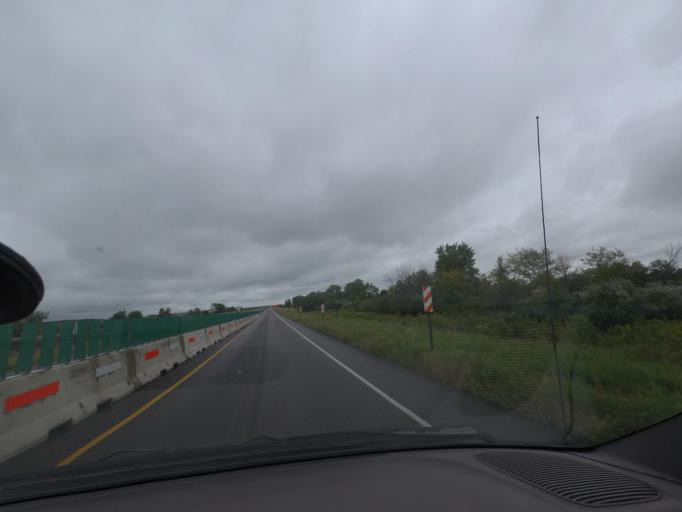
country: US
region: Illinois
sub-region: Piatt County
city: Cerro Gordo
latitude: 40.0018
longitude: -88.7781
